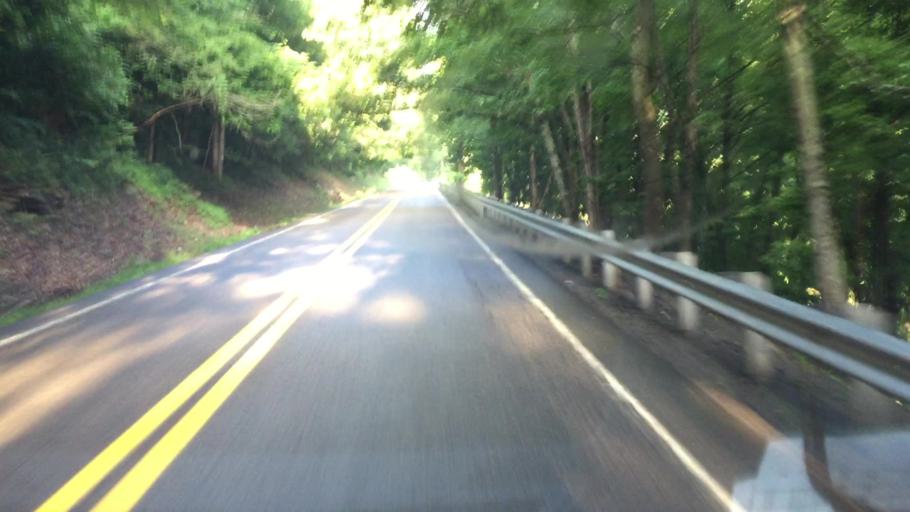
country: US
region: West Virginia
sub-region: Preston County
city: Kingwood
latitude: 39.3258
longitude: -79.8057
